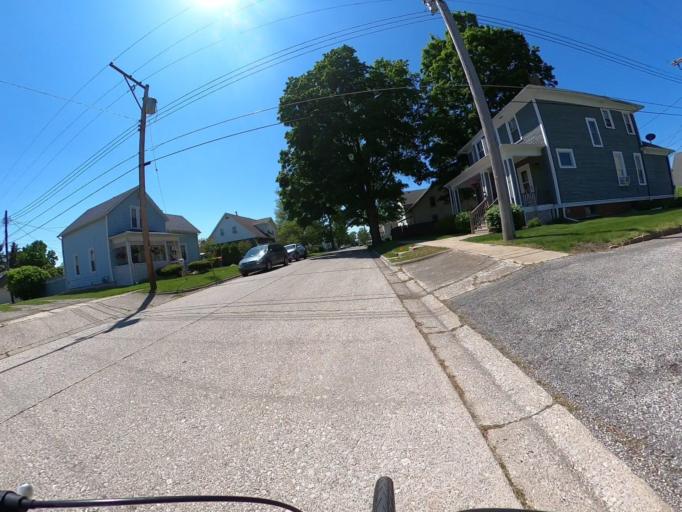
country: US
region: Indiana
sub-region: LaPorte County
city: LaPorte
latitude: 41.6057
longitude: -86.7272
